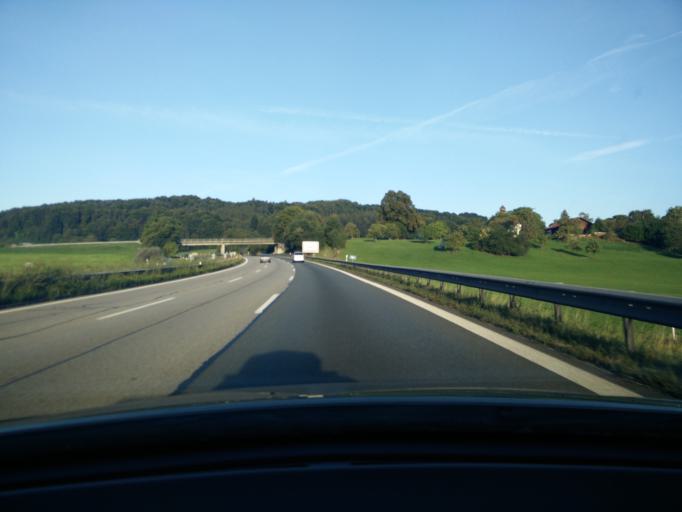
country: DE
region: Bavaria
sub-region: Upper Bavaria
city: Irschenberg
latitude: 47.8273
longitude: 11.9498
